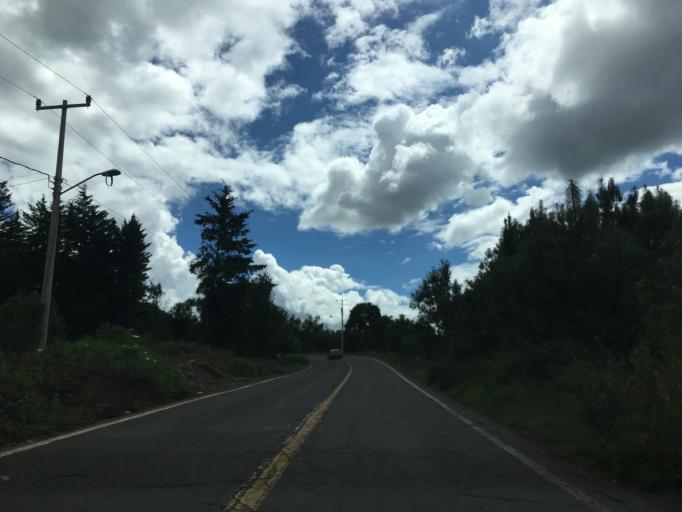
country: MX
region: Michoacan
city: Cheran
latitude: 19.6900
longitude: -101.9648
